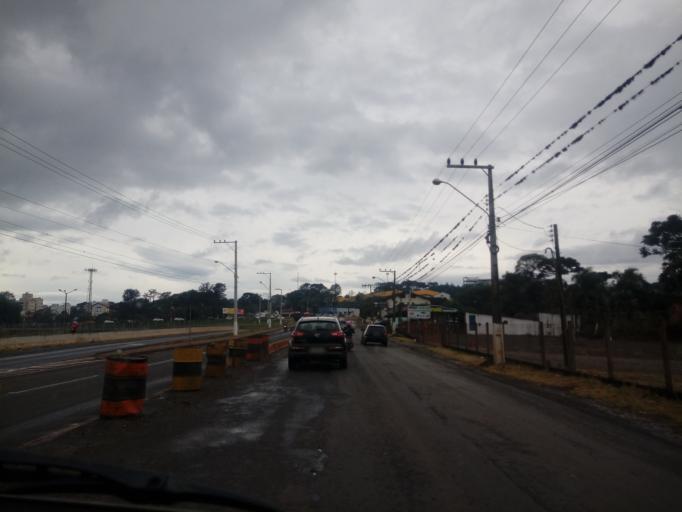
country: BR
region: Santa Catarina
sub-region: Chapeco
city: Chapeco
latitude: -27.0981
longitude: -52.6498
